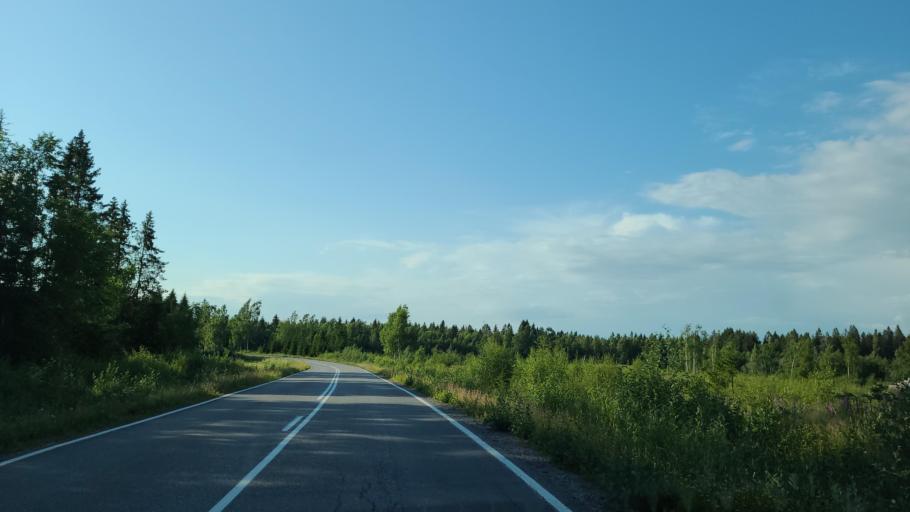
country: FI
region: Ostrobothnia
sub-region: Vaasa
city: Replot
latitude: 63.3190
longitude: 21.3562
